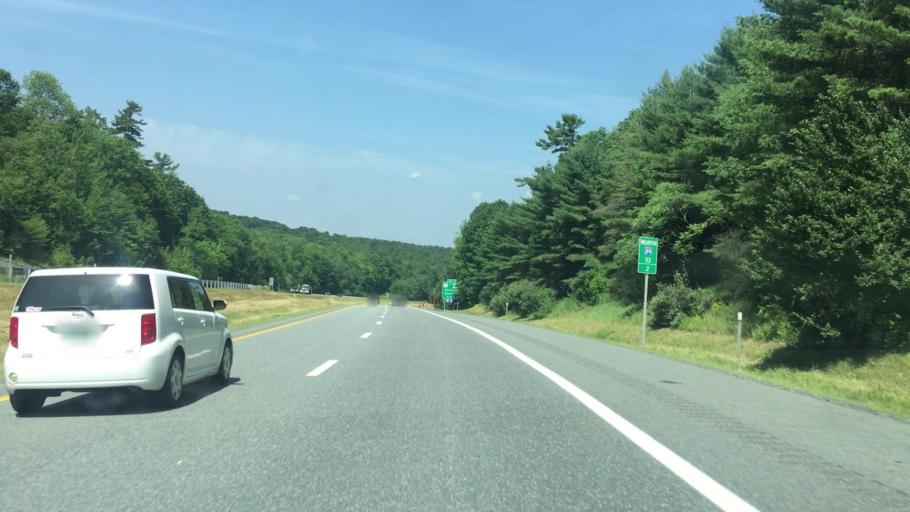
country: US
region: New Hampshire
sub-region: Grafton County
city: Lebanon
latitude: 43.6249
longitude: -72.2018
